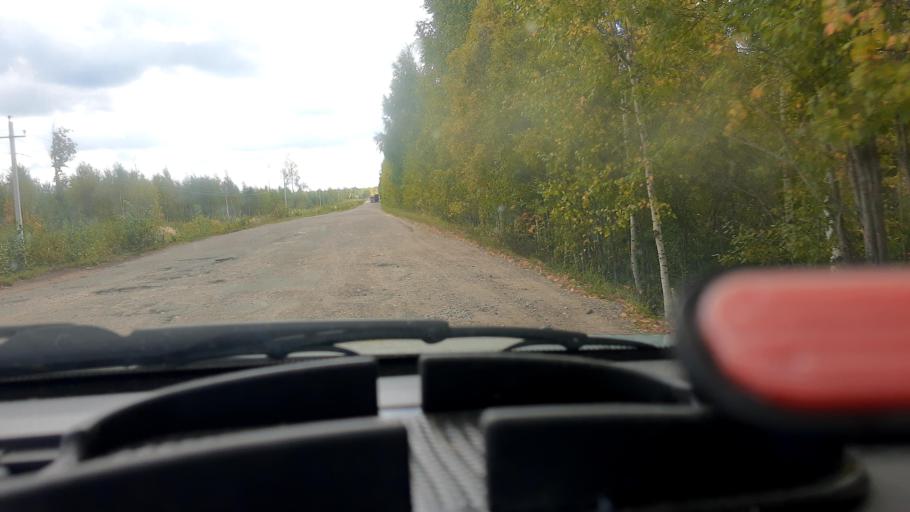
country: RU
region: Mariy-El
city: Kilemary
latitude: 56.8900
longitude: 46.7570
